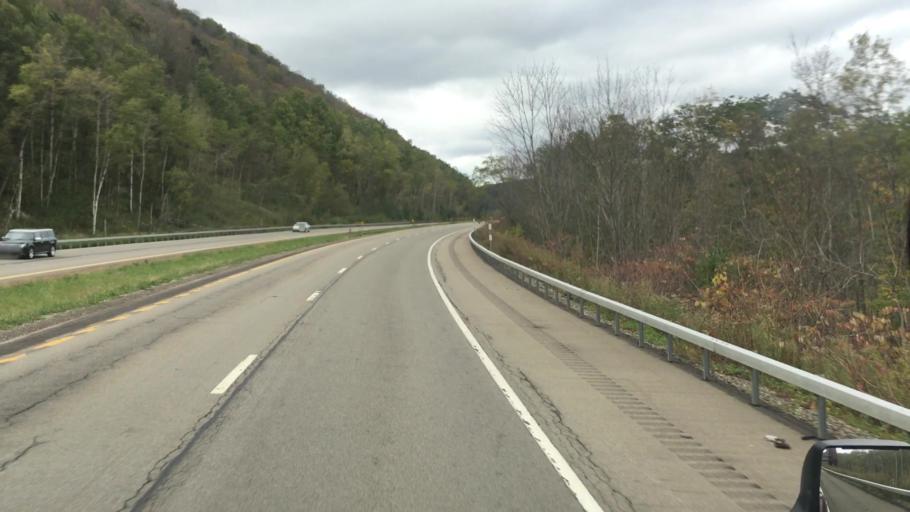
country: US
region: New York
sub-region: Cattaraugus County
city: Salamanca
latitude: 42.1012
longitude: -78.8127
